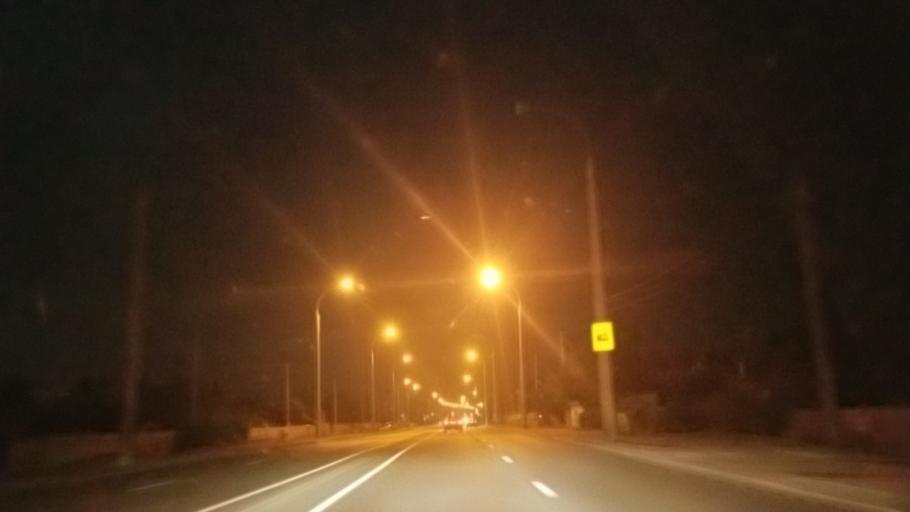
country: BY
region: Brest
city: Brest
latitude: 52.0644
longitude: 23.7373
